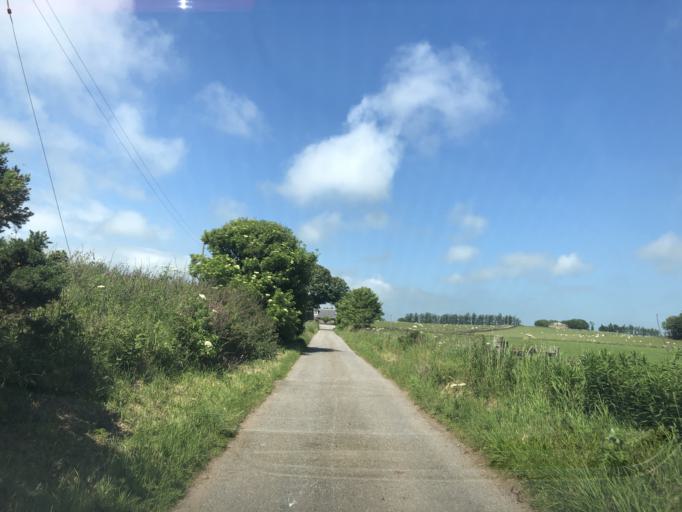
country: GB
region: Scotland
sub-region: Aberdeenshire
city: Stonehaven
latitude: 56.9191
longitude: -2.2080
